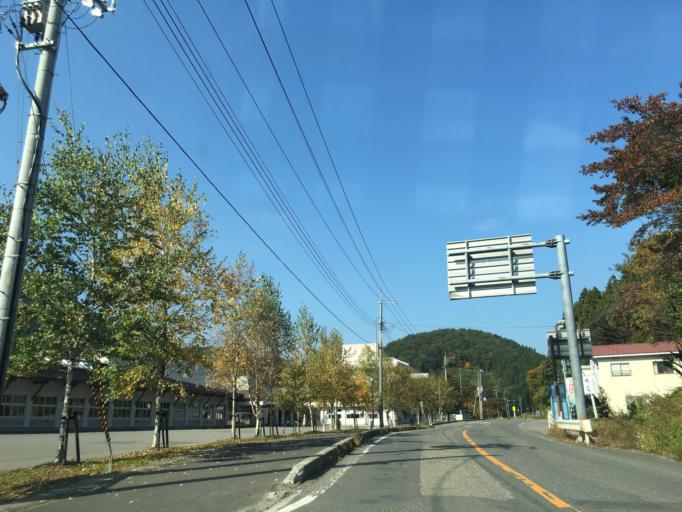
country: JP
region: Fukushima
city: Inawashiro
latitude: 37.3826
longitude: 140.1148
